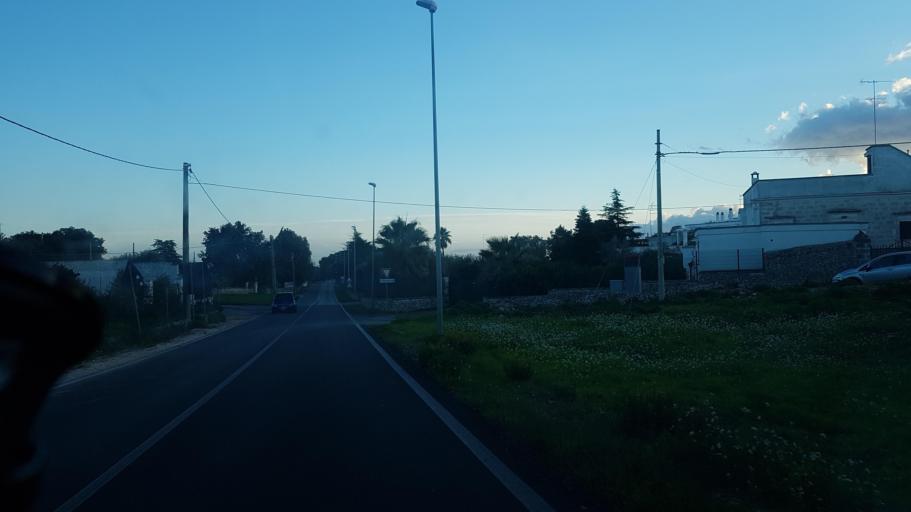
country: IT
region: Apulia
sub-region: Provincia di Brindisi
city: Ostuni
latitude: 40.7168
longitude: 17.5832
